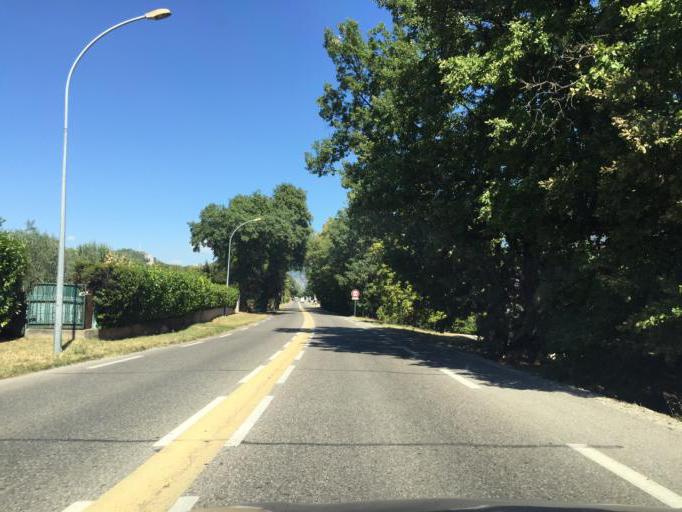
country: FR
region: Provence-Alpes-Cote d'Azur
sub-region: Departement des Alpes-de-Haute-Provence
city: Les Mees
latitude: 44.0697
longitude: 5.9860
